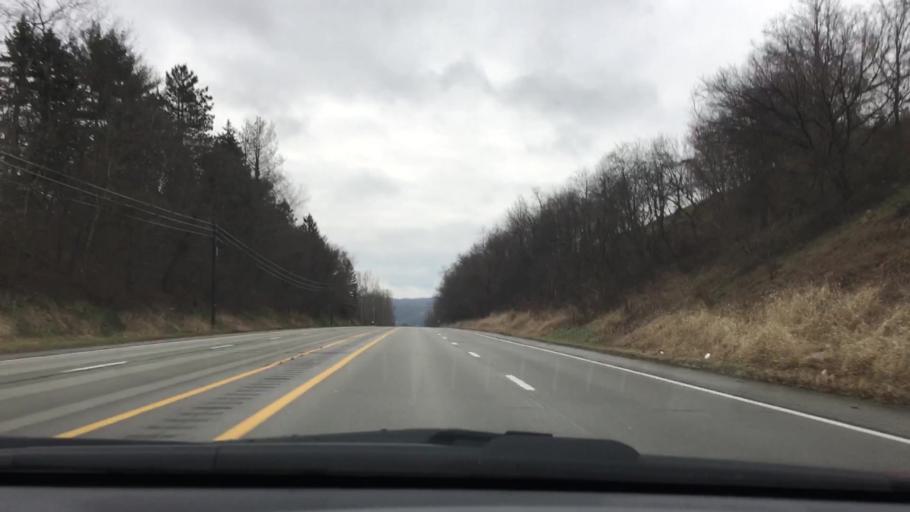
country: US
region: Pennsylvania
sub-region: Fayette County
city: Perryopolis
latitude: 40.1060
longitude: -79.7696
